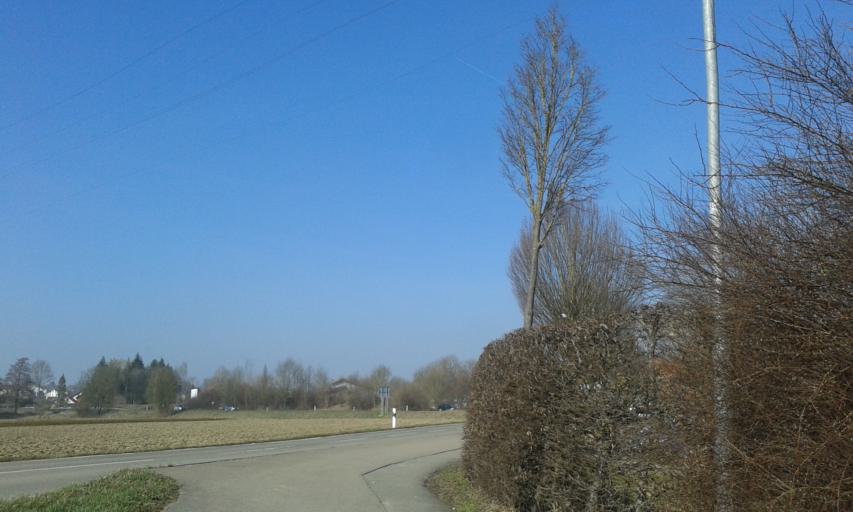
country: DE
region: Baden-Wuerttemberg
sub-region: Tuebingen Region
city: Oberdischingen
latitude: 48.3006
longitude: 9.8443
